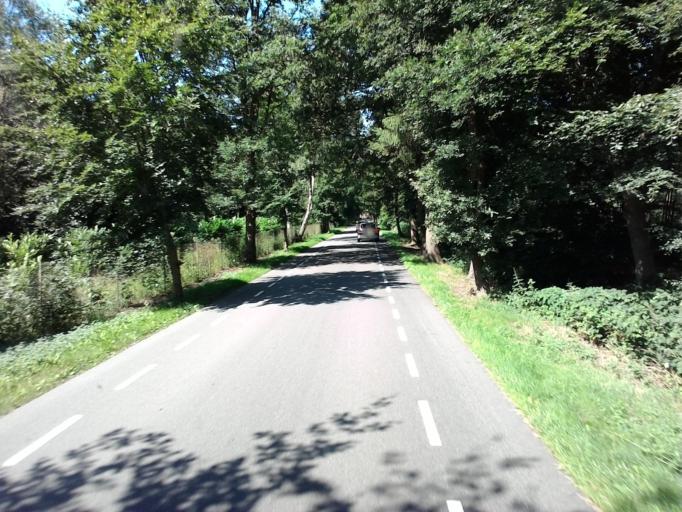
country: NL
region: North Holland
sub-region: Gemeente Hilversum
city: Hilversum
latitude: 52.1750
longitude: 5.2226
